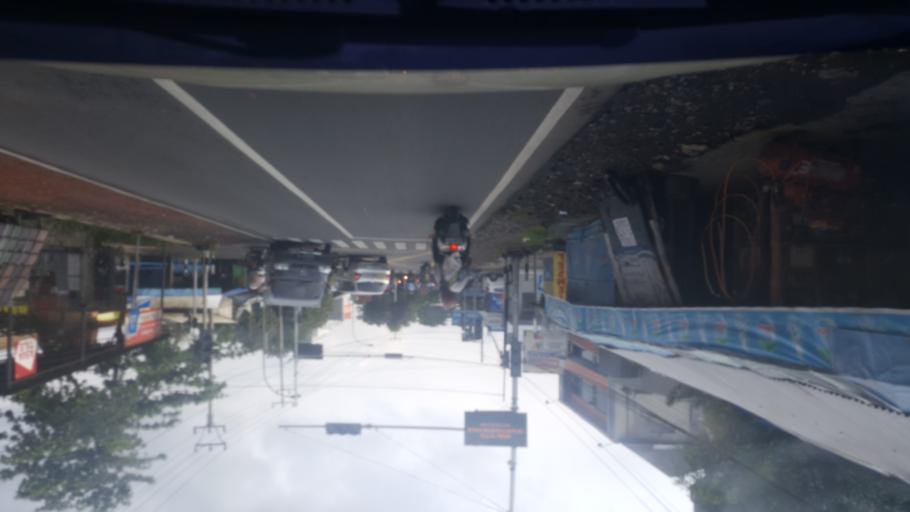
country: ID
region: West Java
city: Jati
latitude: -7.3009
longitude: 108.2026
